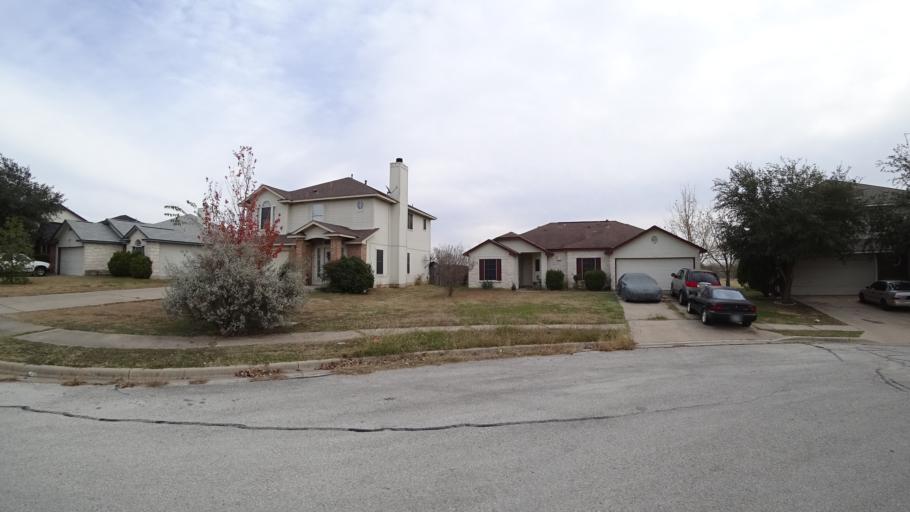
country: US
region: Texas
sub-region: Travis County
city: Garfield
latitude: 30.1545
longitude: -97.6430
